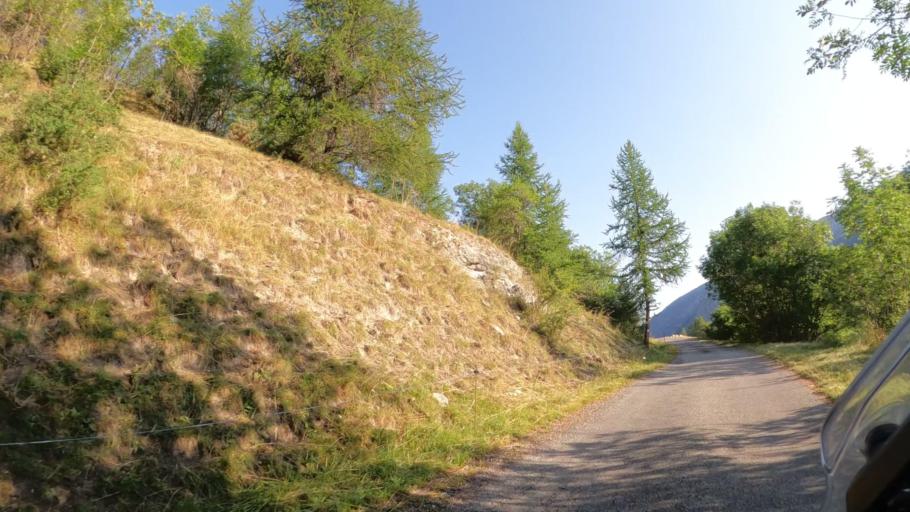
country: FR
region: Provence-Alpes-Cote d'Azur
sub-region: Departement des Hautes-Alpes
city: Guillestre
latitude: 44.6046
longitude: 6.6843
